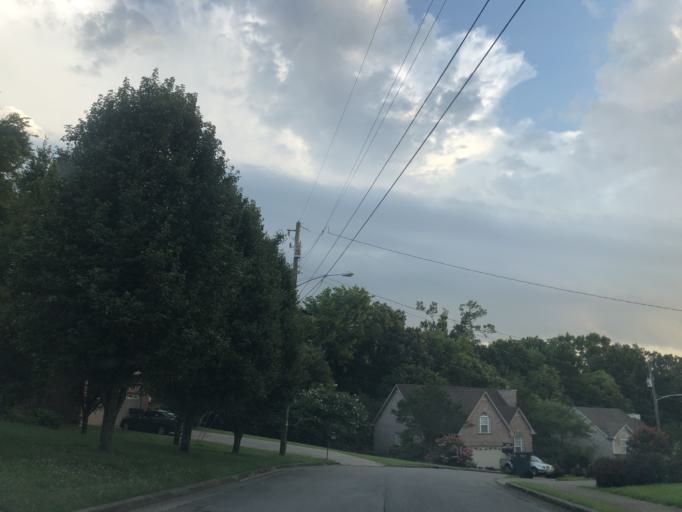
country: US
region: Tennessee
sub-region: Davidson County
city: Lakewood
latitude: 36.1440
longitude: -86.6348
